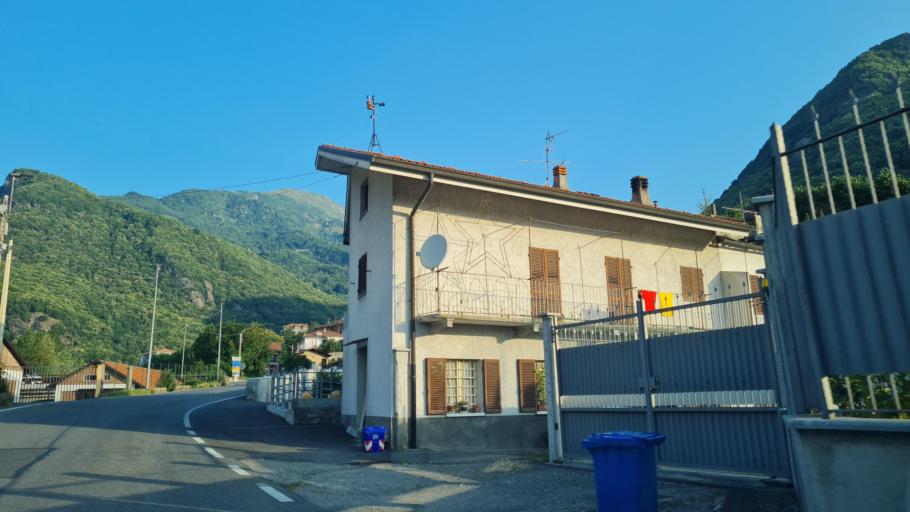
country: IT
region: Piedmont
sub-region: Provincia di Torino
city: Pont-Canavese
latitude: 45.4214
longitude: 7.6025
